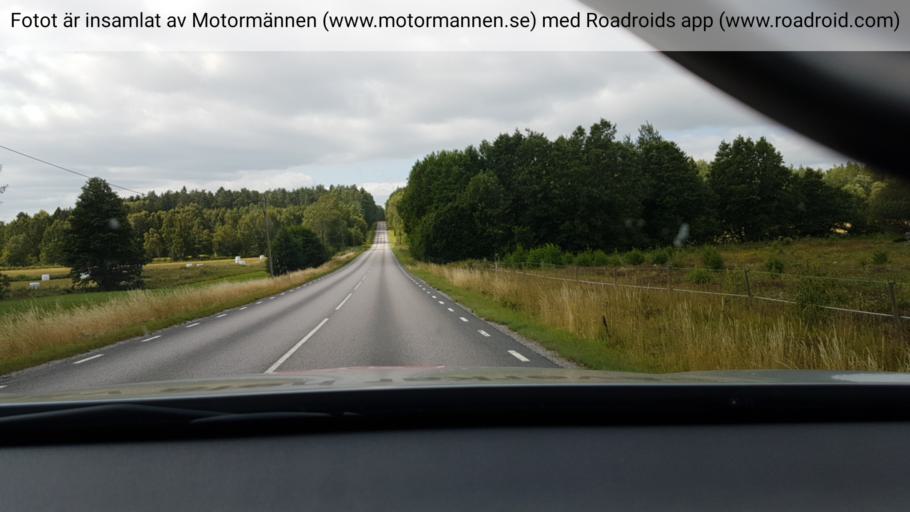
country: SE
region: Stockholm
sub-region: Norrtalje Kommun
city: Rimbo
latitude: 59.7094
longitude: 18.4233
